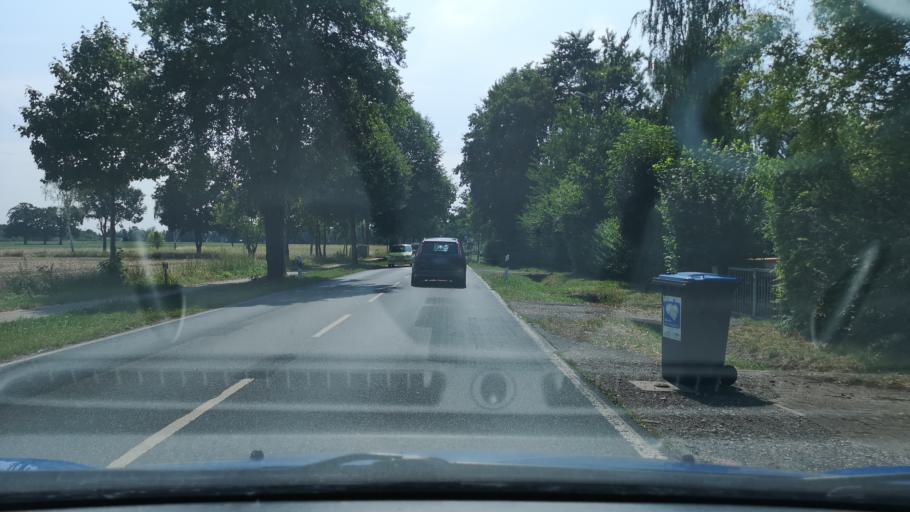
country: DE
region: Lower Saxony
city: Isernhagen Farster Bauerschaft
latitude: 52.4456
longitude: 9.7997
